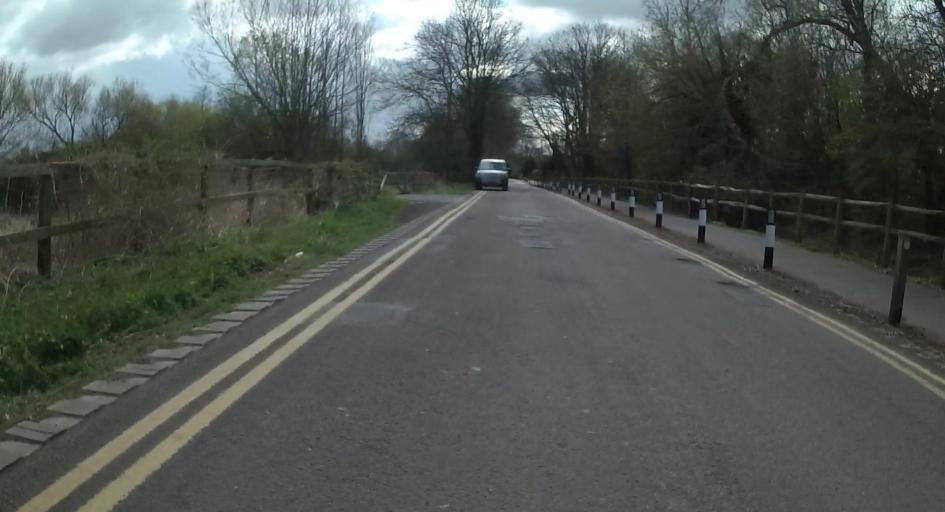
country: GB
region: England
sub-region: Surrey
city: Shepperton
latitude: 51.3864
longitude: -0.4582
